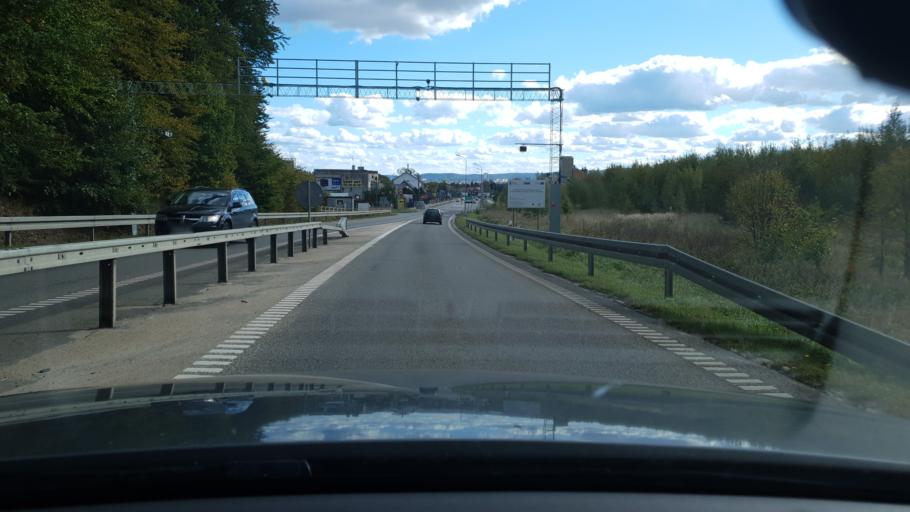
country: PL
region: Pomeranian Voivodeship
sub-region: Powiat wejherowski
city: Reda
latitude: 54.6199
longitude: 18.3411
